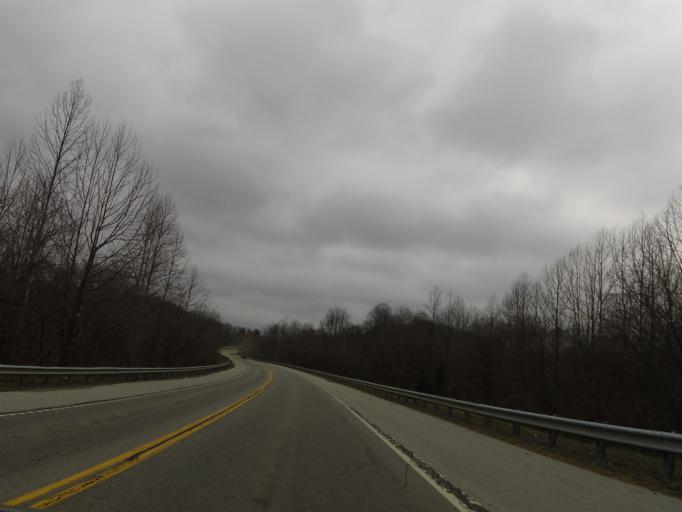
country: US
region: Tennessee
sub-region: Scott County
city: Huntsville
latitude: 36.3818
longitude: -84.5562
